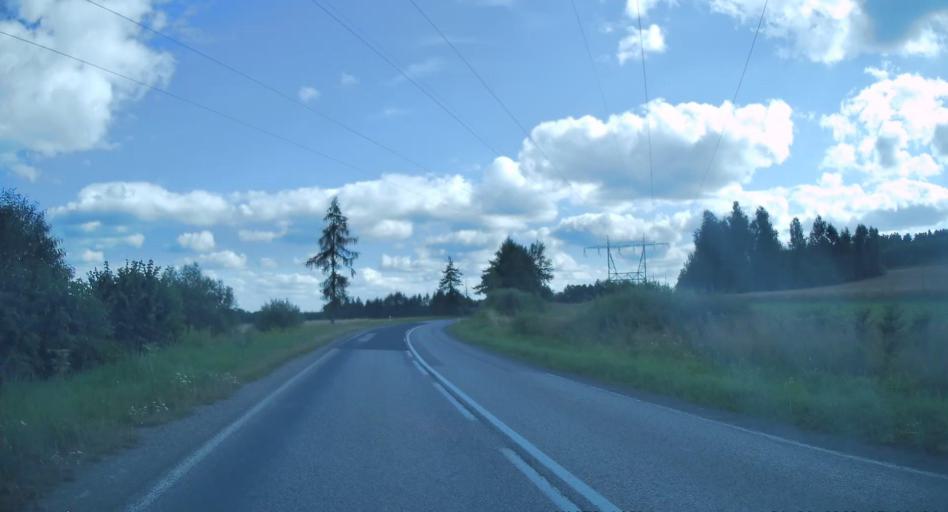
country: PL
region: Swietokrzyskie
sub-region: Powiat kielecki
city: Lagow
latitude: 50.8118
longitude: 21.0796
